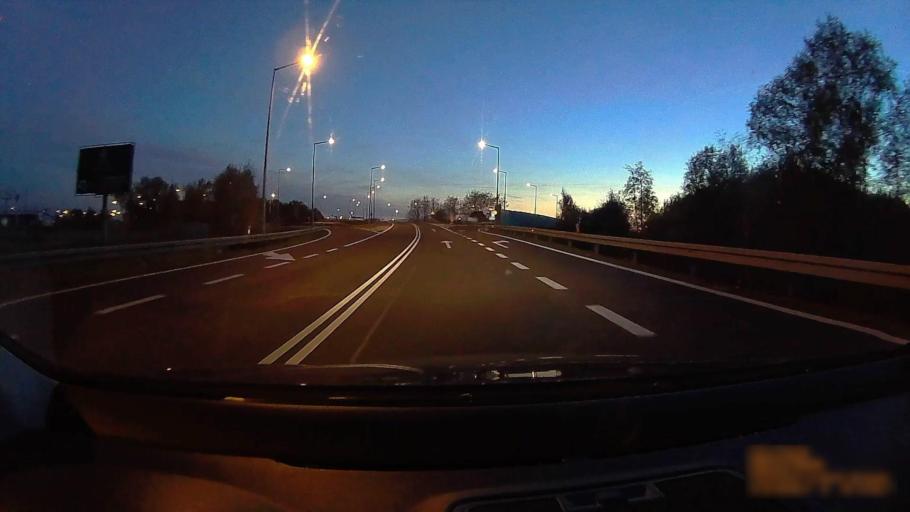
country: PL
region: Greater Poland Voivodeship
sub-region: Powiat koninski
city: Stare Miasto
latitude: 52.1658
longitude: 18.2080
